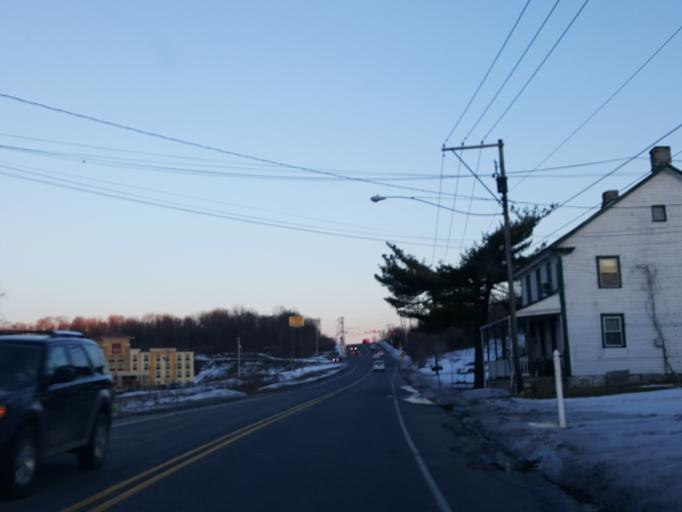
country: US
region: Pennsylvania
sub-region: Dauphin County
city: Rutherford
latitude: 40.2628
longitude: -76.7489
